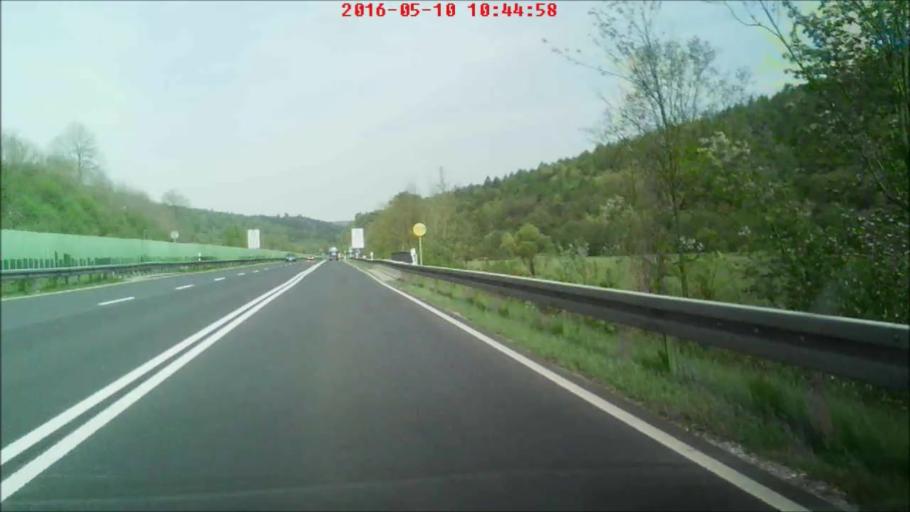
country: DE
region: Hesse
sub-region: Regierungsbezirk Kassel
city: Burghaun
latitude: 50.7260
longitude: 9.7048
